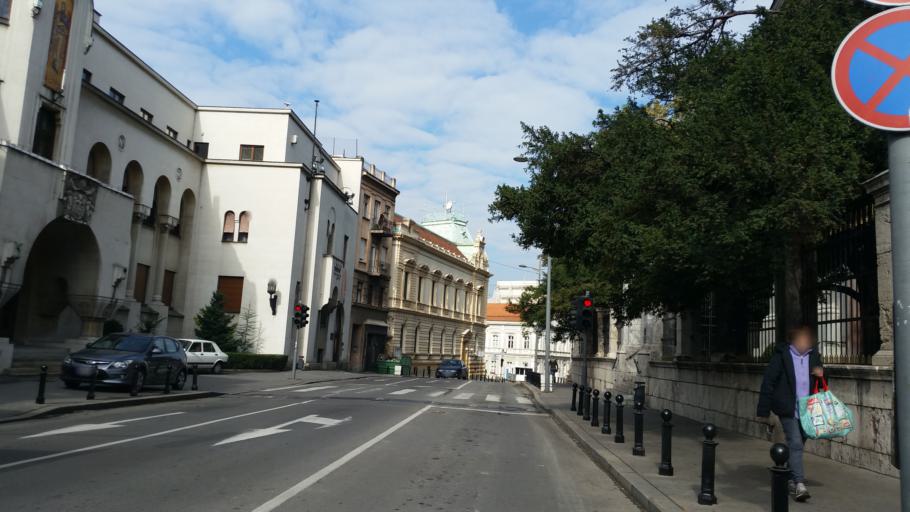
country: RS
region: Central Serbia
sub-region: Belgrade
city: Stari Grad
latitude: 44.8177
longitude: 20.4522
